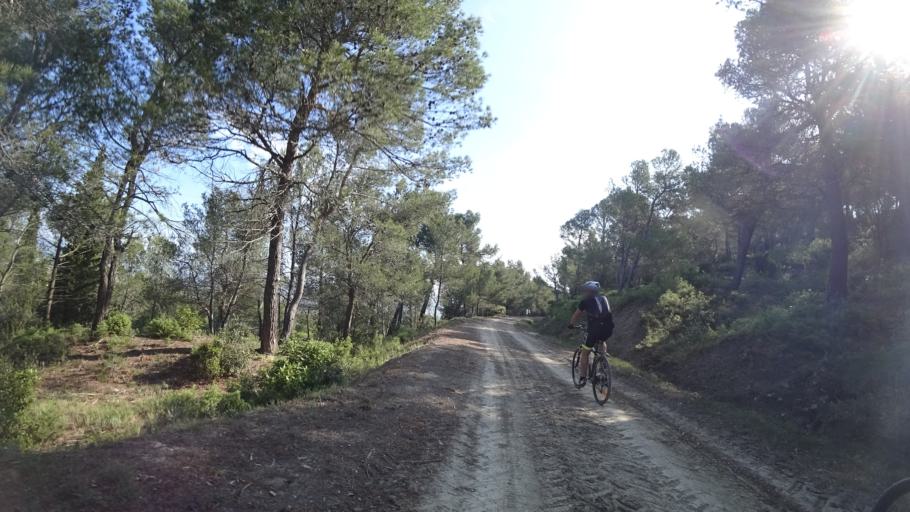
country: FR
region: Languedoc-Roussillon
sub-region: Departement de l'Herault
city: Olonzac
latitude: 43.2491
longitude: 2.7279
